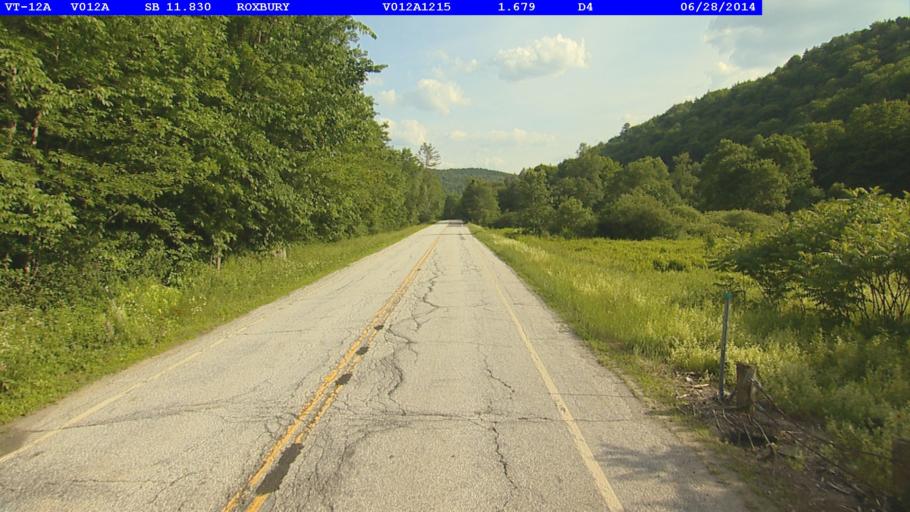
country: US
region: Vermont
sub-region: Washington County
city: Northfield
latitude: 44.0528
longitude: -72.7438
